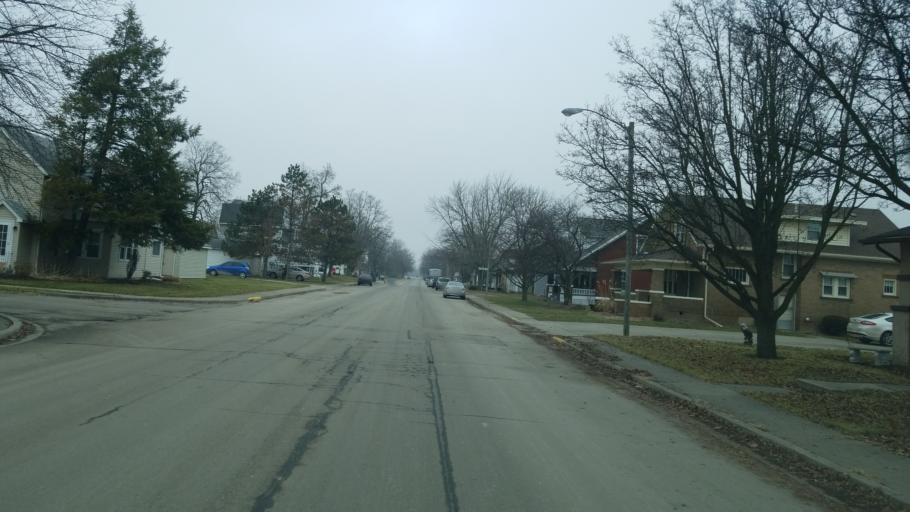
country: US
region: Indiana
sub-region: Adams County
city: Berne
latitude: 40.6603
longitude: -84.9513
